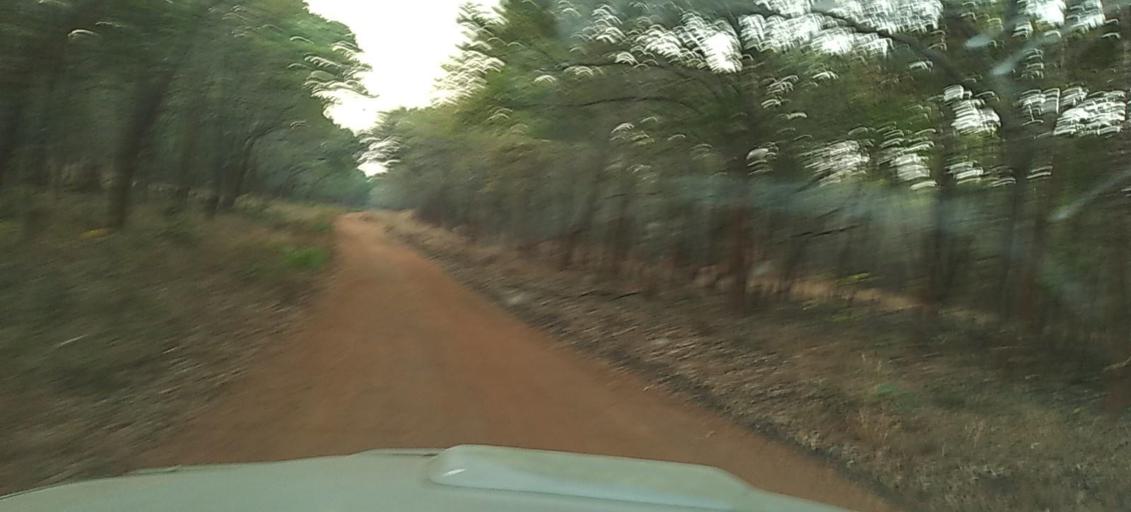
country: ZM
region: North-Western
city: Kasempa
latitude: -13.0845
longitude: 26.3963
